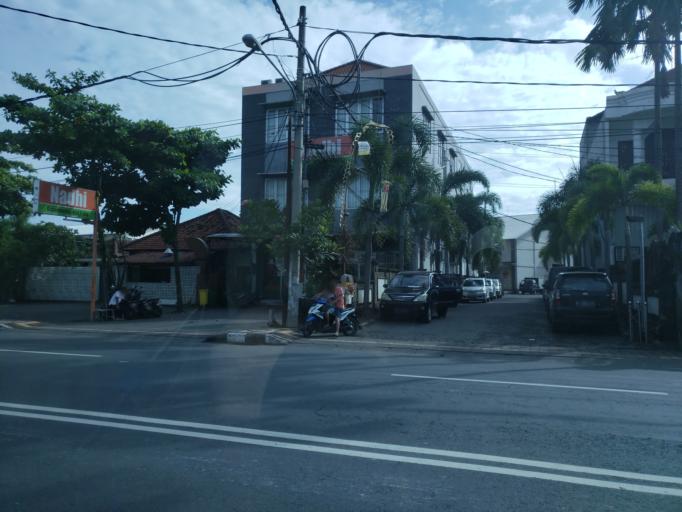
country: ID
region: Bali
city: Denpasar
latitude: -8.6705
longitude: 115.1912
